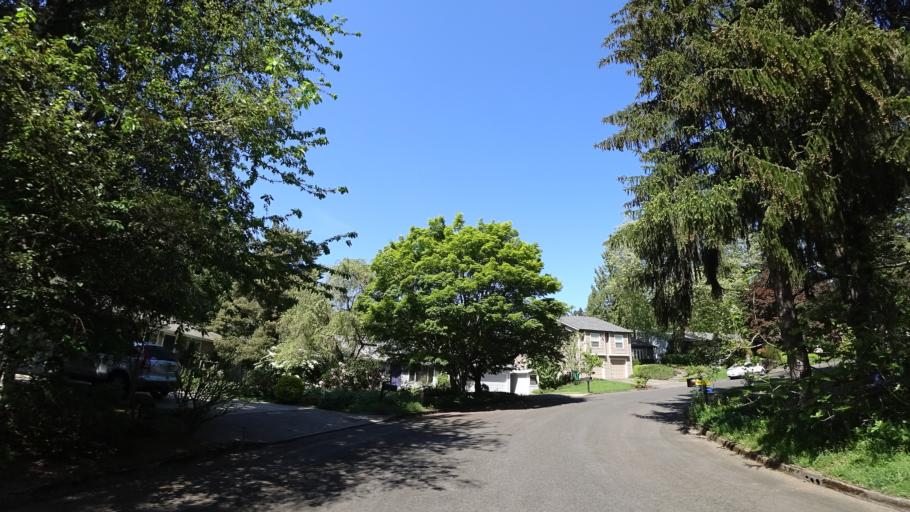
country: US
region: Oregon
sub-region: Washington County
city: Raleigh Hills
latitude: 45.4891
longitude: -122.7368
